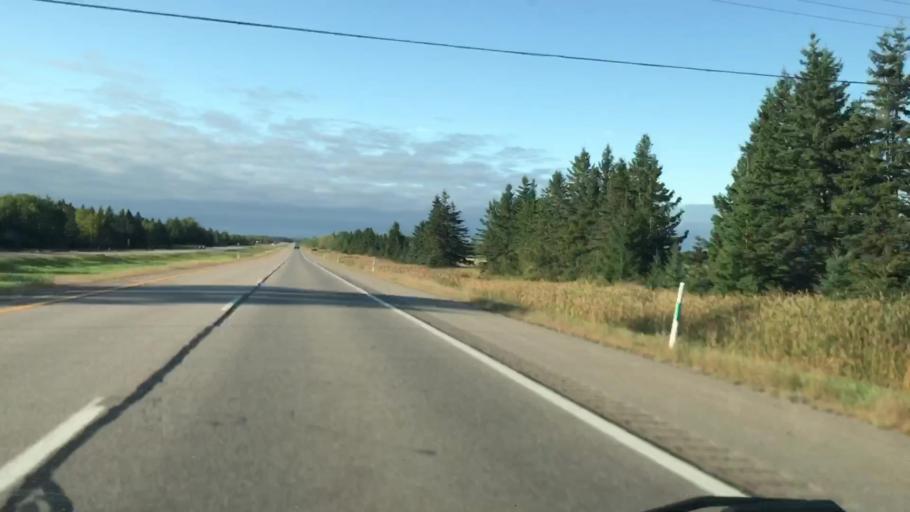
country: US
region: Michigan
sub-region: Chippewa County
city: Sault Ste. Marie
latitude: 46.4190
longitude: -84.3955
